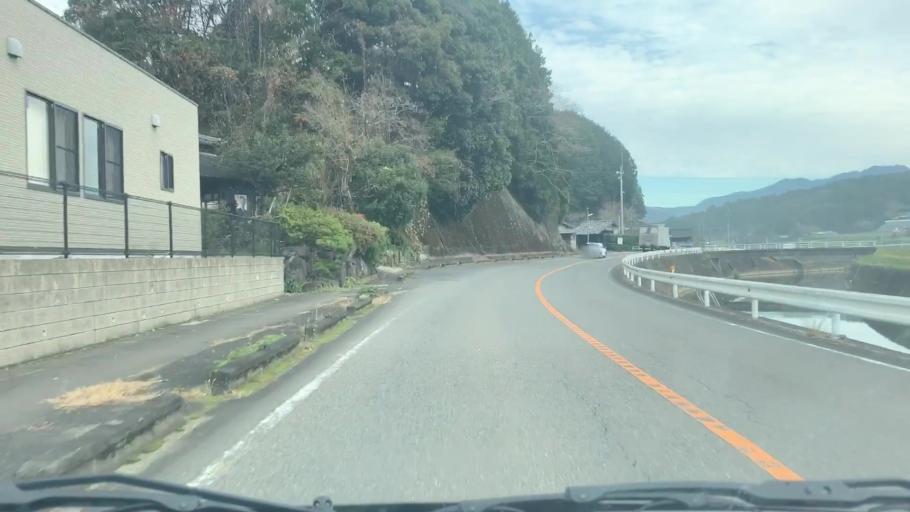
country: JP
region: Saga Prefecture
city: Takeocho-takeo
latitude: 33.2302
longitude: 129.9644
